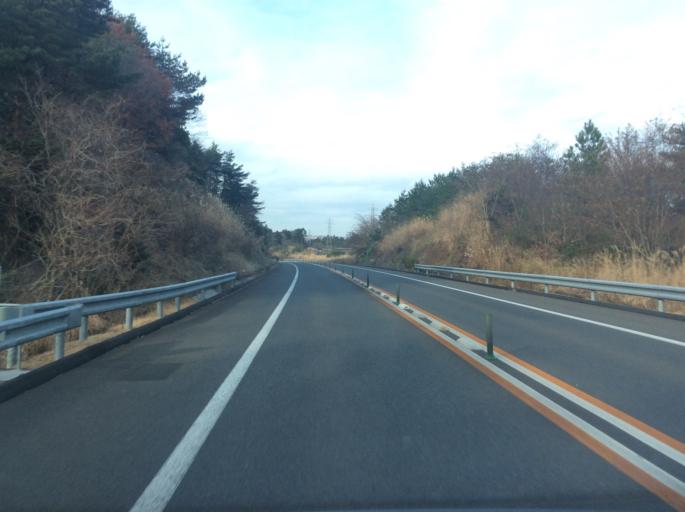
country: JP
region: Fukushima
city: Namie
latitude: 37.2584
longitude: 140.9912
